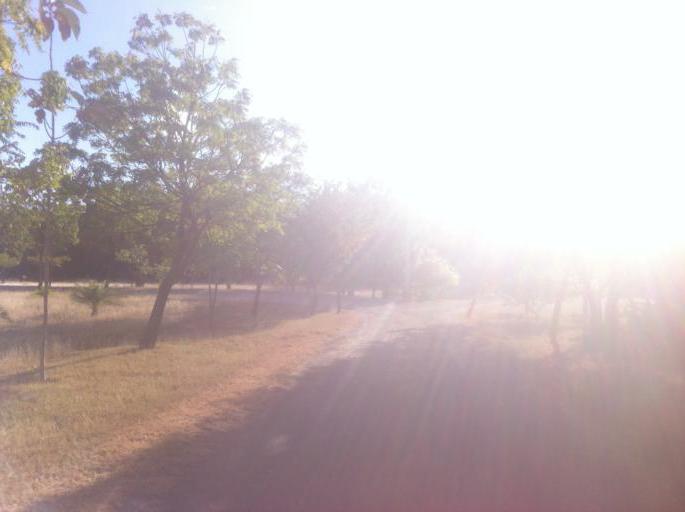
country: NI
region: Managua
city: Carlos Fonseca Amador
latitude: 11.9174
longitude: -86.5971
